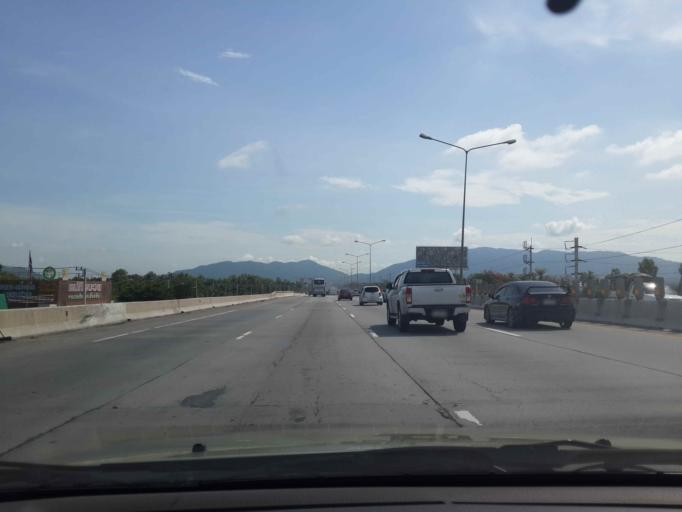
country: TH
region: Chon Buri
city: Si Racha
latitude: 13.1800
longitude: 100.9951
